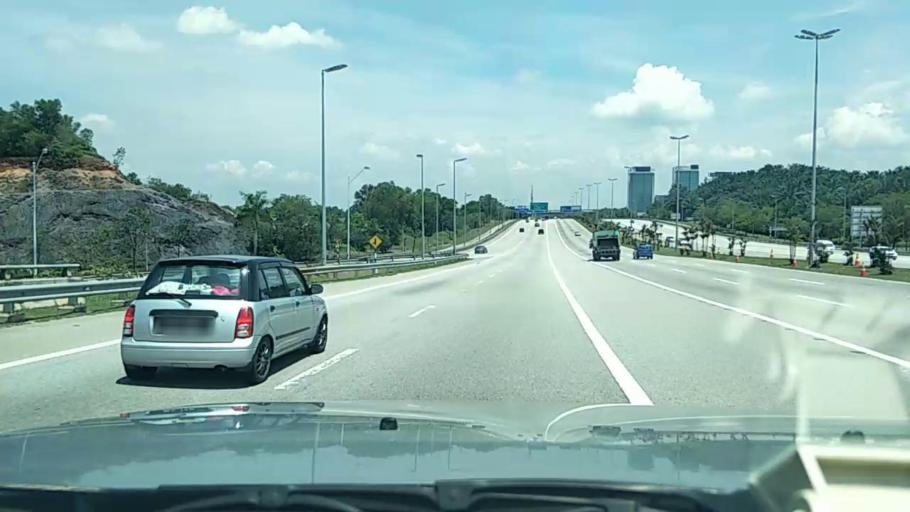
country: MY
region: Putrajaya
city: Putrajaya
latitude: 2.9360
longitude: 101.6685
